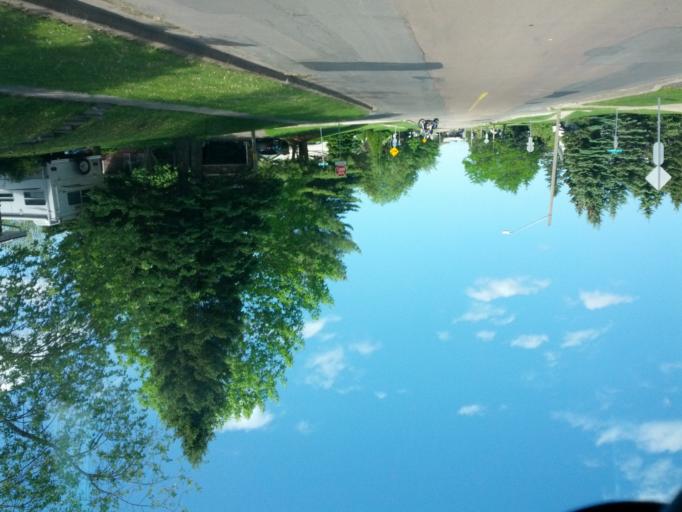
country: CA
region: New Brunswick
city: Moncton
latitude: 46.1253
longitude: -64.8514
